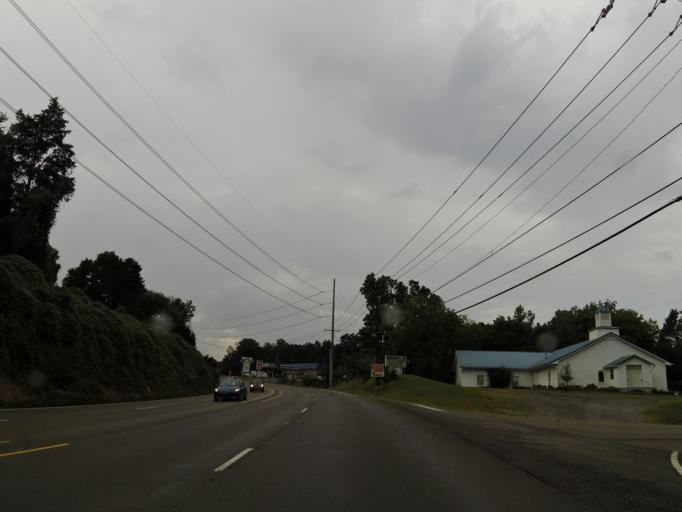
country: US
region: Tennessee
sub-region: Sevier County
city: Seymour
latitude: 35.8978
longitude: -83.8127
